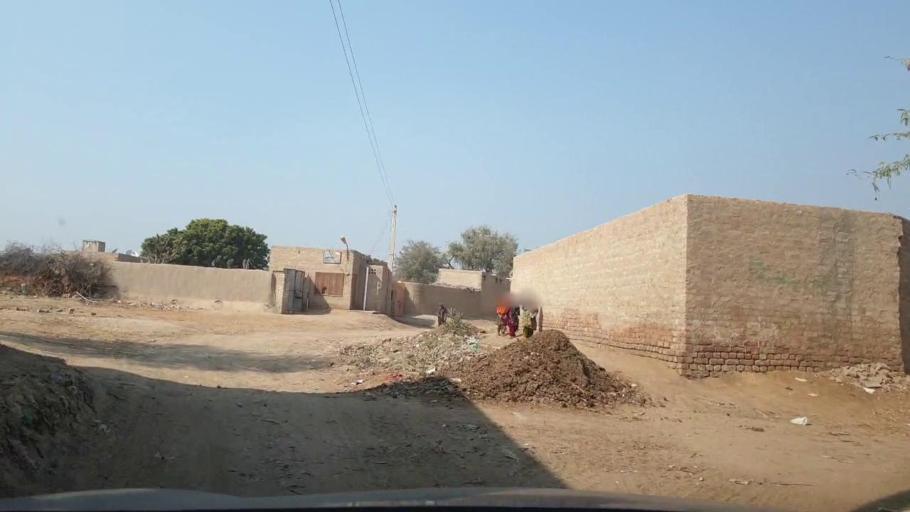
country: PK
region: Sindh
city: Tando Allahyar
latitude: 25.5910
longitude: 68.8283
